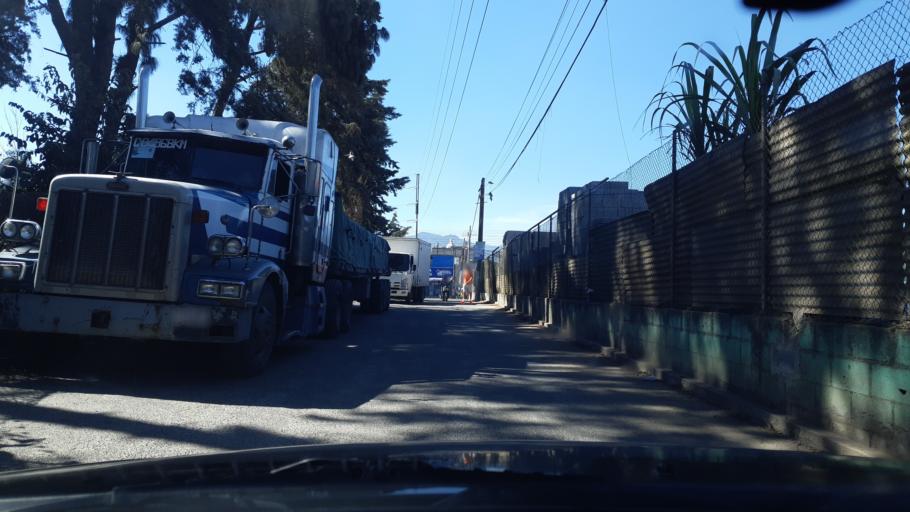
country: GT
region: Chimaltenango
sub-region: Municipio de Chimaltenango
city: Chimaltenango
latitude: 14.6584
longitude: -90.8069
